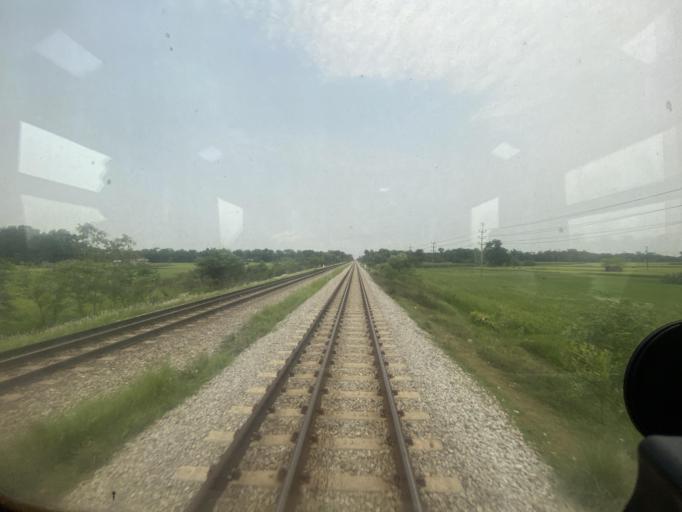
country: BD
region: Chittagong
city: Laksham
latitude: 23.3151
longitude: 91.1408
